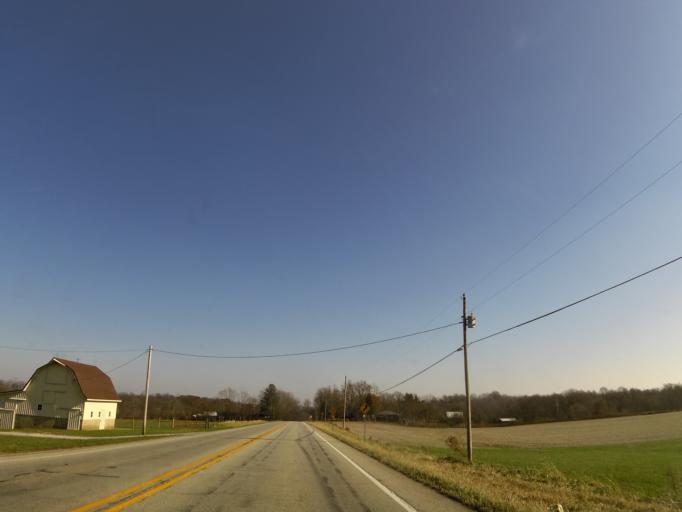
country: US
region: Indiana
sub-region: Fayette County
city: Connersville
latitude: 39.6316
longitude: -85.2275
